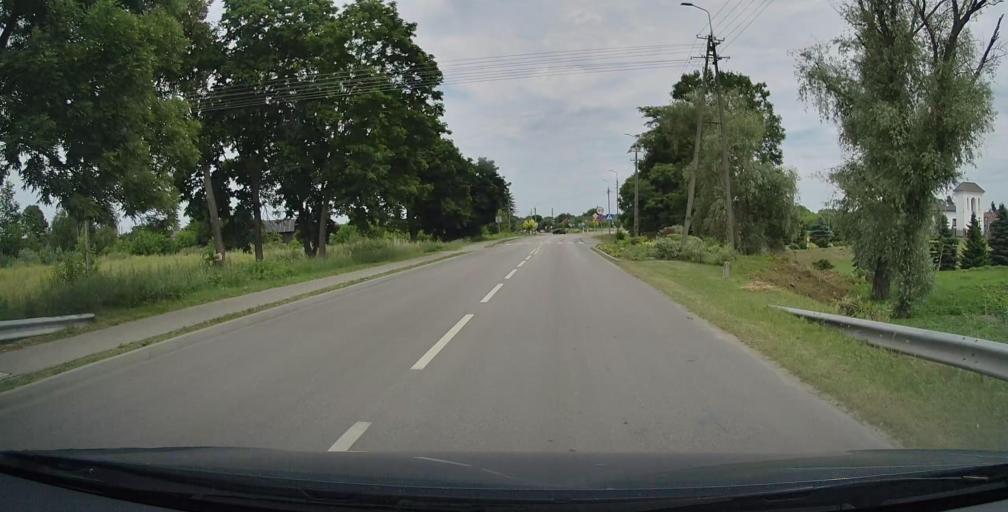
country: PL
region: Lublin Voivodeship
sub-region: Powiat bialski
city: Terespol
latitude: 52.0762
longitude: 23.6264
